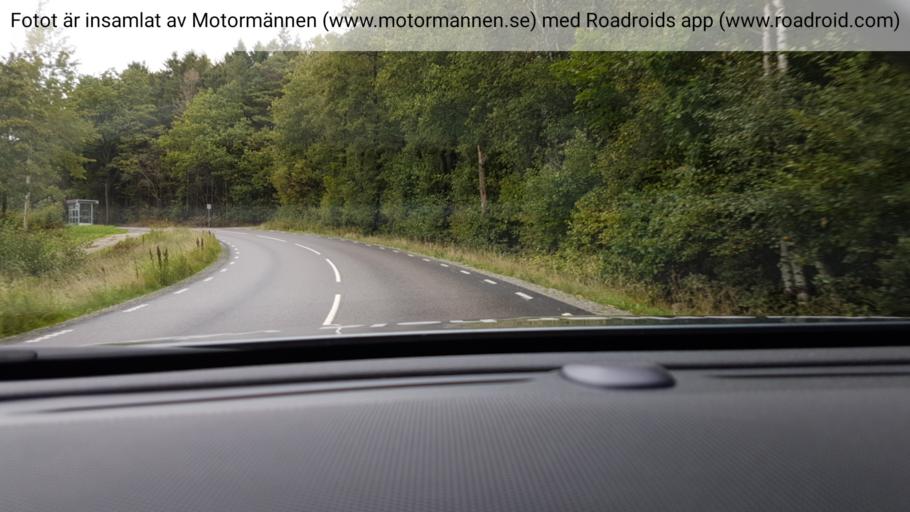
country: SE
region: Vaestra Goetaland
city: Svanesund
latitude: 58.1152
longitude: 11.8550
